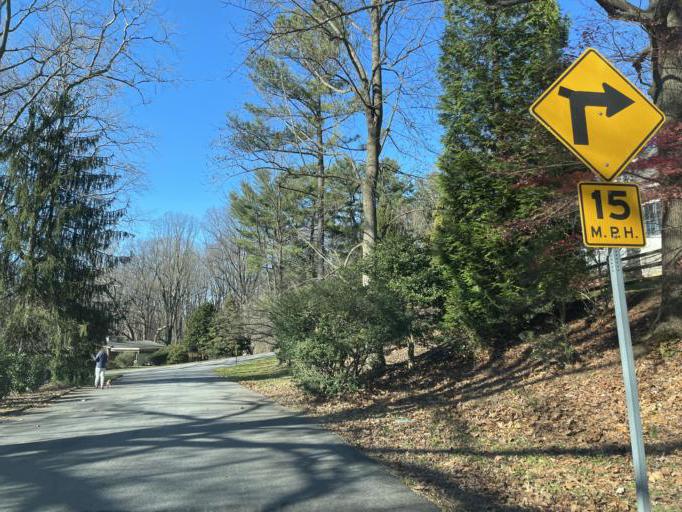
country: US
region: Maryland
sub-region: Baltimore County
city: Mays Chapel
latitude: 39.3937
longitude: -76.6560
